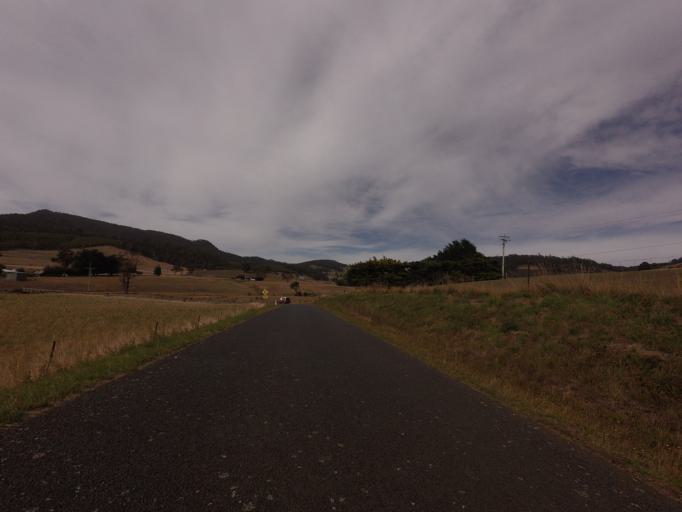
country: AU
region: Tasmania
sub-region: Sorell
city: Sorell
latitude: -42.4802
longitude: 147.5748
